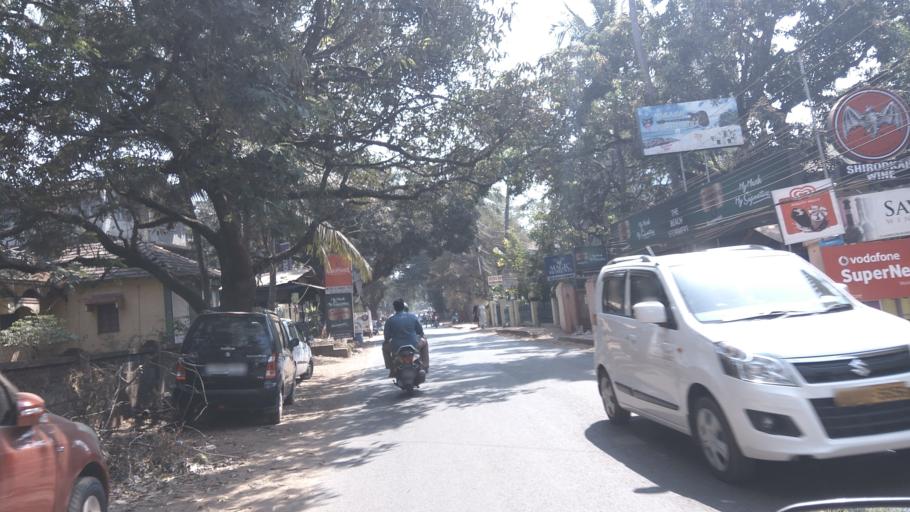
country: IN
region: Goa
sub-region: North Goa
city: Candolim
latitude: 15.5260
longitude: 73.7658
